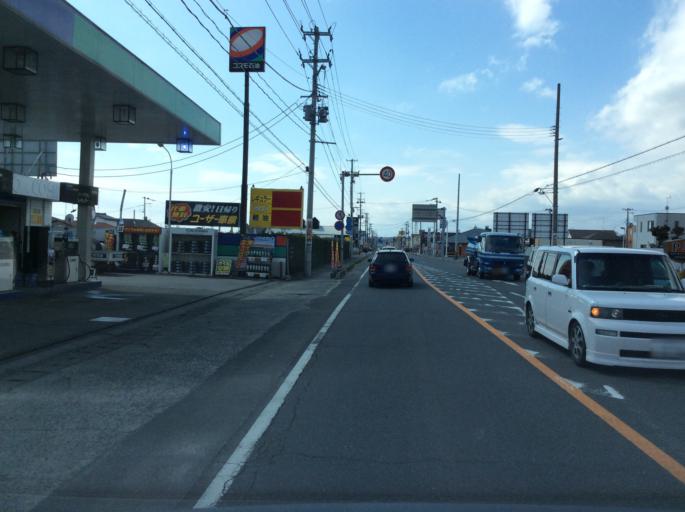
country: JP
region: Fukushima
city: Iwaki
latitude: 36.9538
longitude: 140.8659
